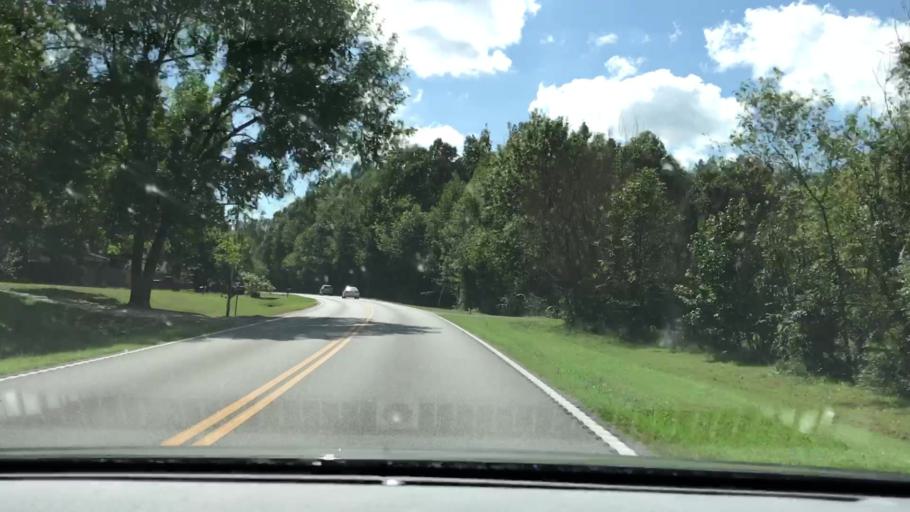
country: US
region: Kentucky
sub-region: McCracken County
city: Reidland
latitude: 36.9686
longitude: -88.5156
